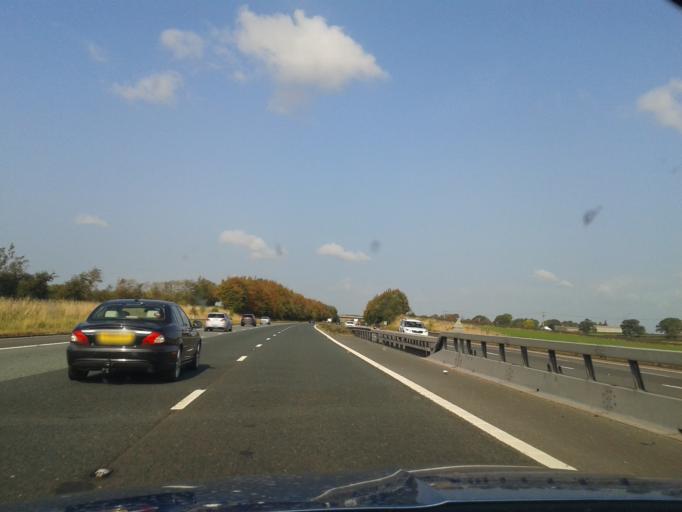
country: GB
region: England
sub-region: Cumbria
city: Scotby
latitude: 54.8124
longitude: -2.8809
